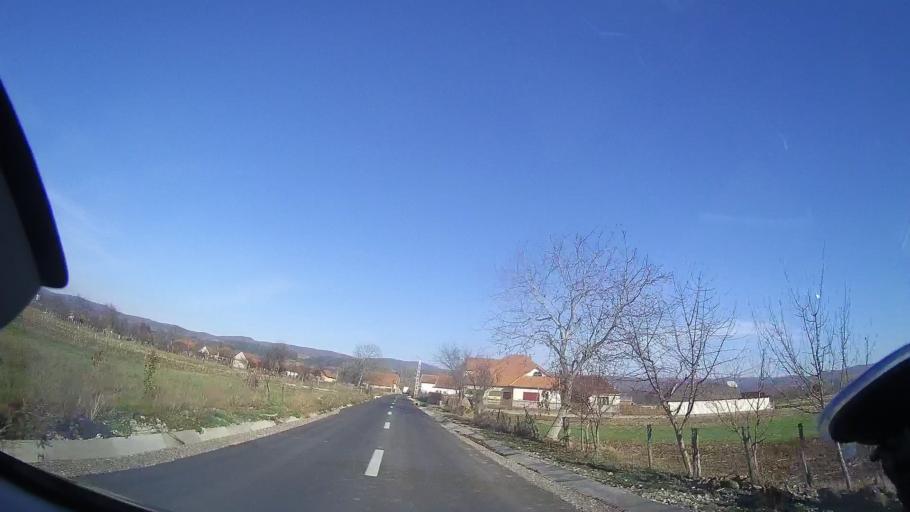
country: RO
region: Bihor
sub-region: Comuna Auseu
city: Auseu
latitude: 47.0188
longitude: 22.4931
